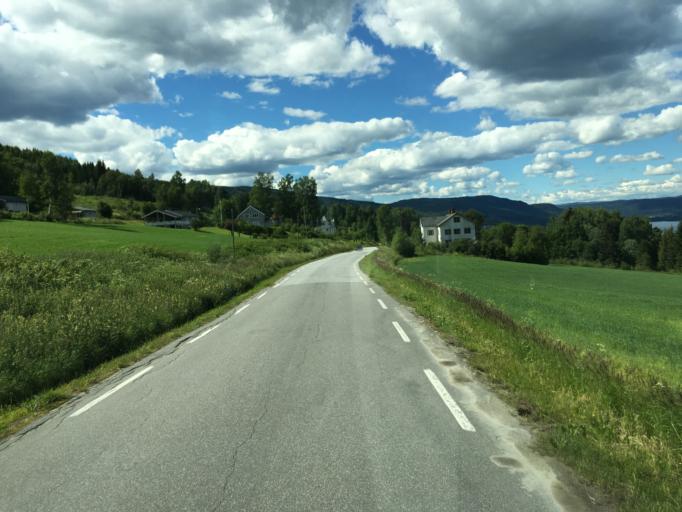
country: NO
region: Oppland
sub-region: Sondre Land
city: Hov
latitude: 60.7010
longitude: 10.2780
